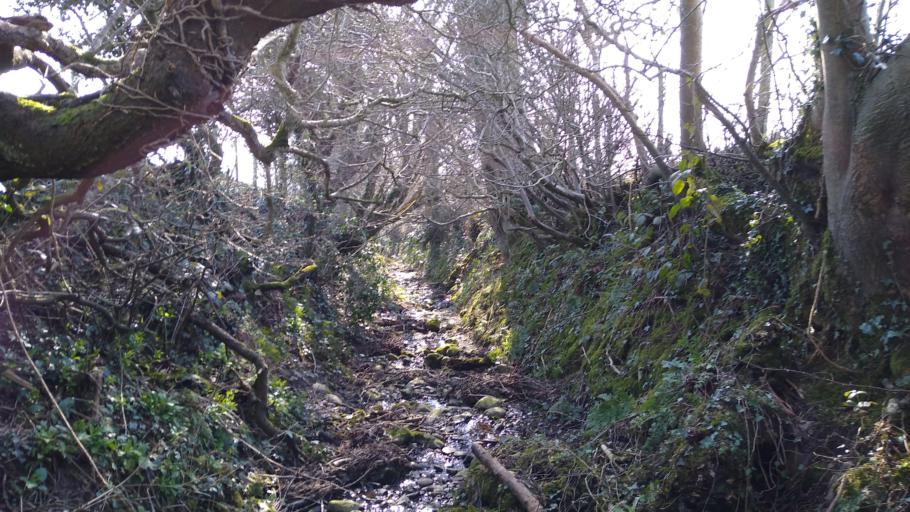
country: GB
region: England
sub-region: Cumbria
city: Cockermouth
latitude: 54.6725
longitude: -3.3910
